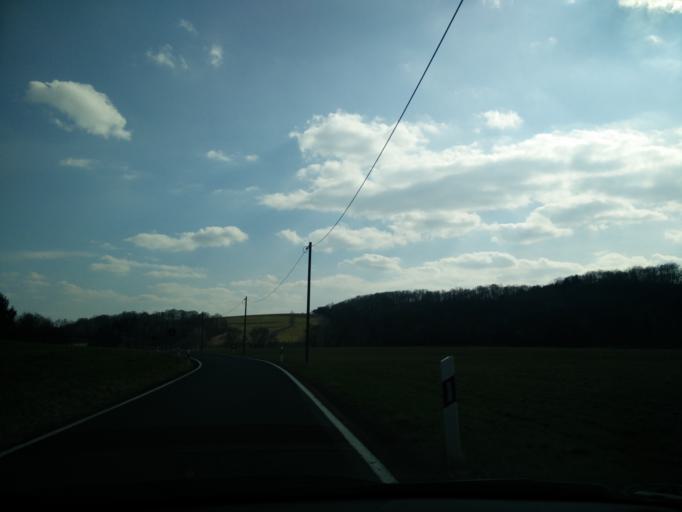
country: DE
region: Saxony
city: Colditz
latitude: 51.1009
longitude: 12.8058
